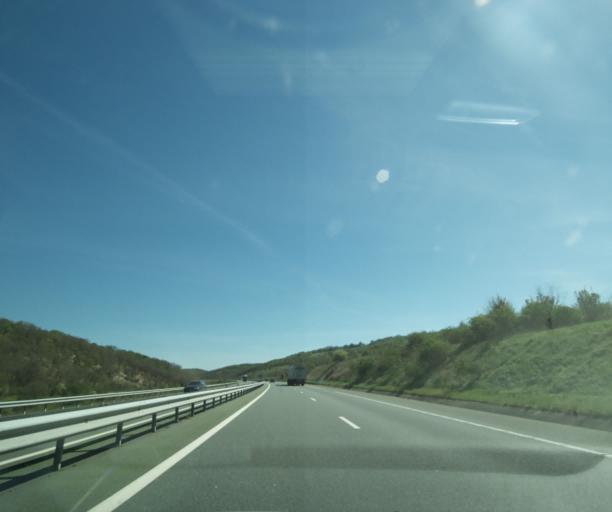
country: FR
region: Midi-Pyrenees
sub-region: Departement du Lot
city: Le Vigan
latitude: 44.7516
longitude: 1.5413
